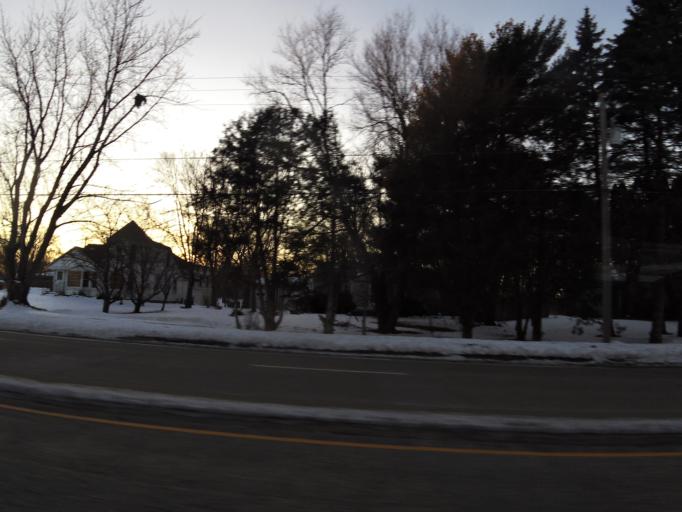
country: US
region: Minnesota
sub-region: Ramsey County
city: White Bear Lake
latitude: 45.0514
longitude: -93.0153
